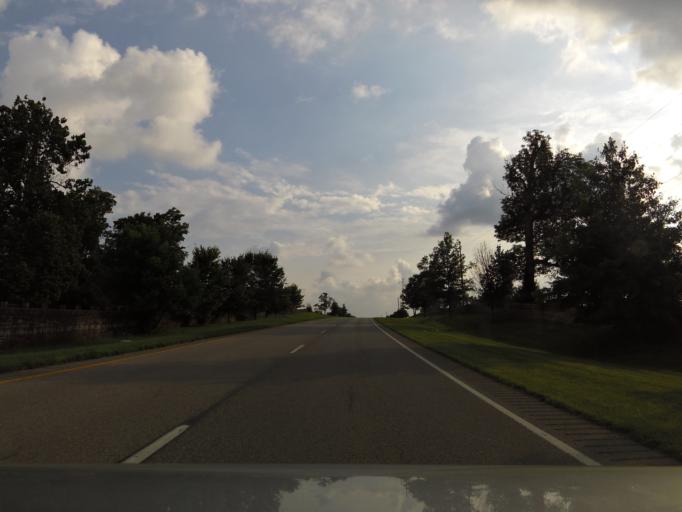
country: US
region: Kentucky
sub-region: Fayette County
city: Lexington-Fayette
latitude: 38.1170
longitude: -84.3937
